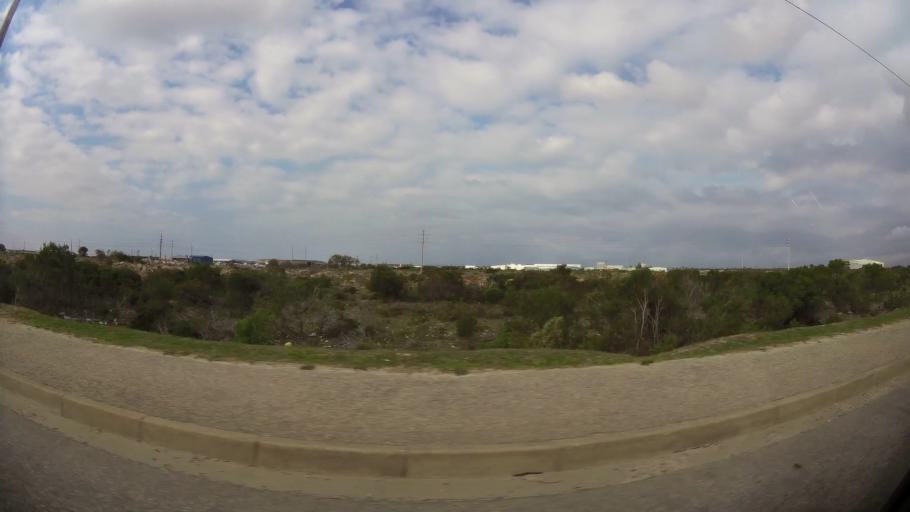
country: ZA
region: Eastern Cape
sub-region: Nelson Mandela Bay Metropolitan Municipality
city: Port Elizabeth
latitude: -33.8067
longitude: 25.6192
